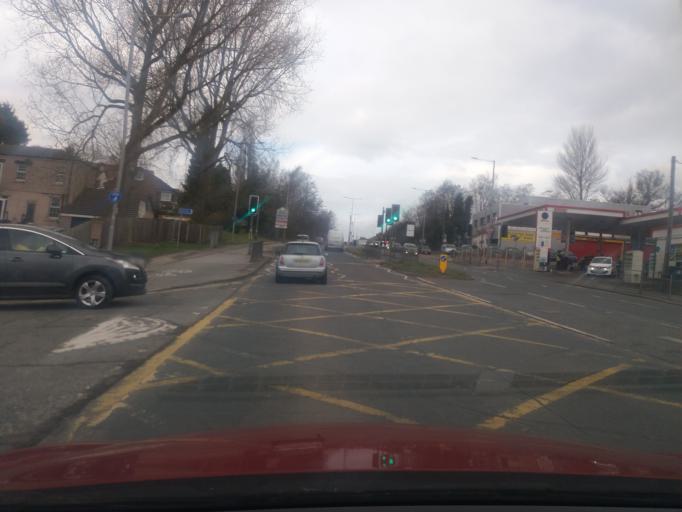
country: GB
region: England
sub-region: Lancashire
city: Preston
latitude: 53.7534
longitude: -2.6801
